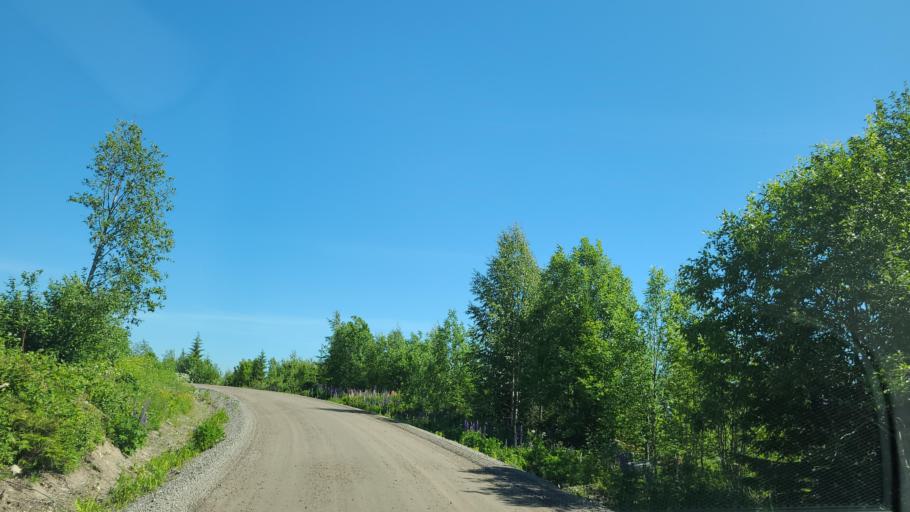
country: SE
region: Vaesterbotten
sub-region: Bjurholms Kommun
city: Bjurholm
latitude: 63.6737
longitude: 19.0286
